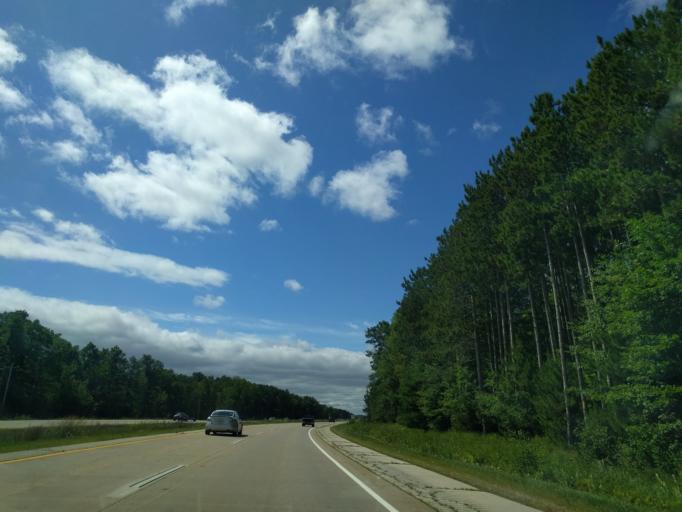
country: US
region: Wisconsin
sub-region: Oconto County
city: Oconto
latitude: 44.8514
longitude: -87.9008
